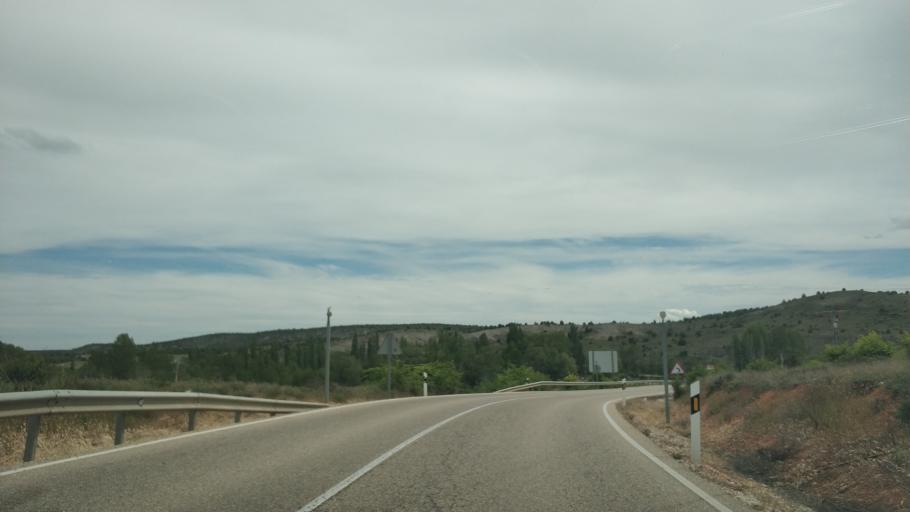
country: ES
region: Castille and Leon
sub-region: Provincia de Soria
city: El Burgo de Osma
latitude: 41.5840
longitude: -3.0410
